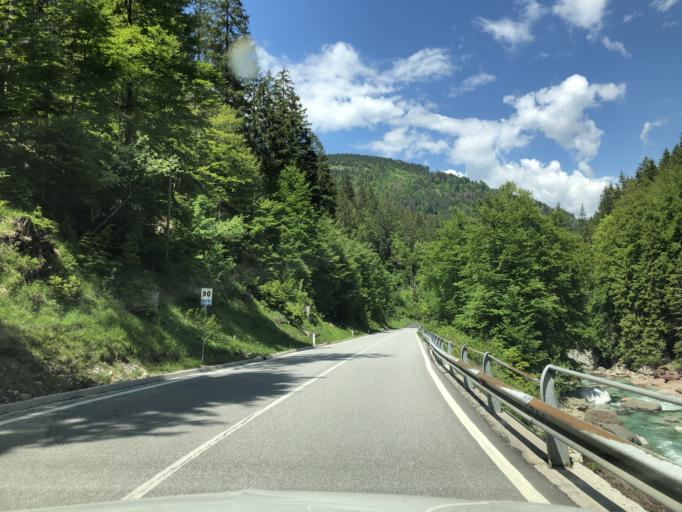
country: IT
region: Friuli Venezia Giulia
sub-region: Provincia di Udine
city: Tarvisio
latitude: 46.4742
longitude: 13.5727
